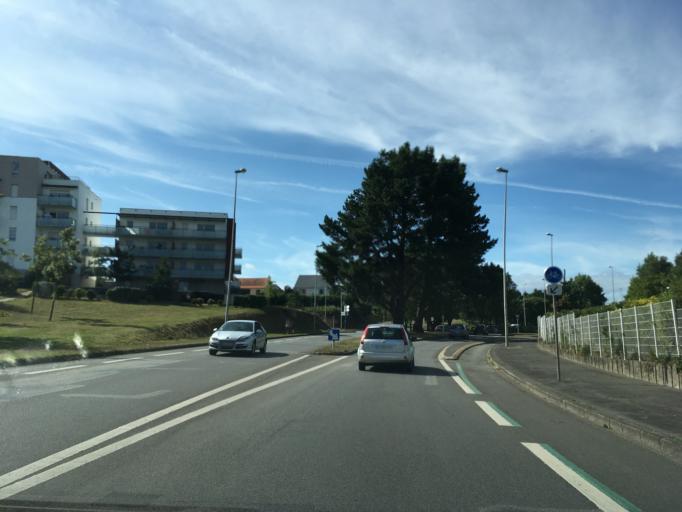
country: FR
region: Brittany
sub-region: Departement du Morbihan
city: Lorient
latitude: 47.7533
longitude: -3.3829
